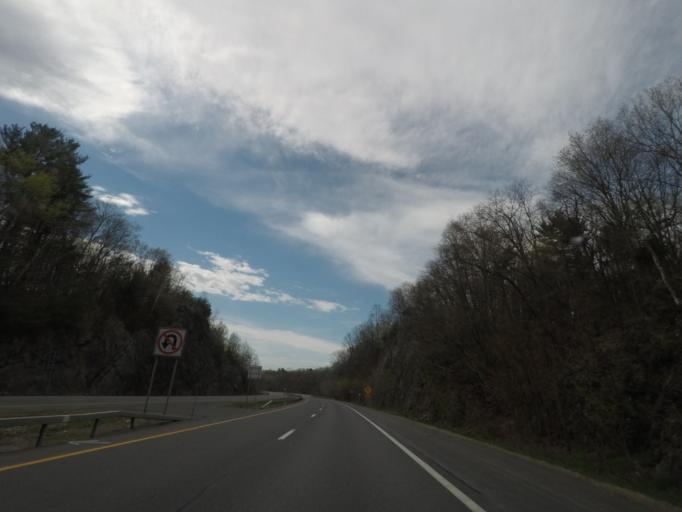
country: US
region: New York
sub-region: Greene County
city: Jefferson Heights
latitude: 42.2471
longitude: -73.8938
